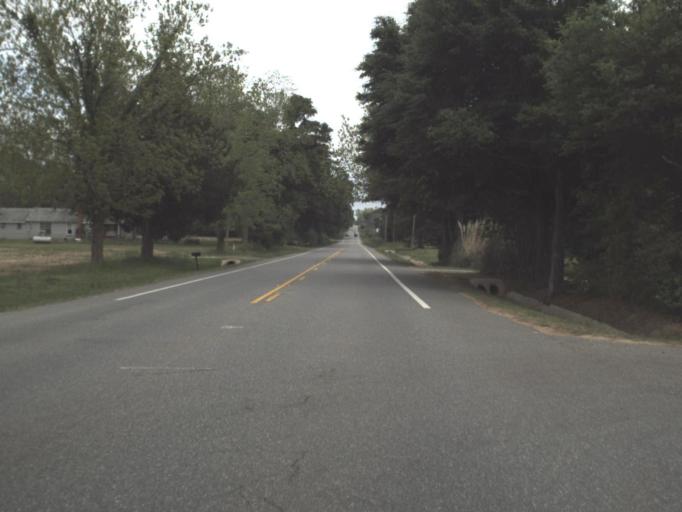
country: US
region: Florida
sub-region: Santa Rosa County
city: Point Baker
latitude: 30.8492
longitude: -87.0523
